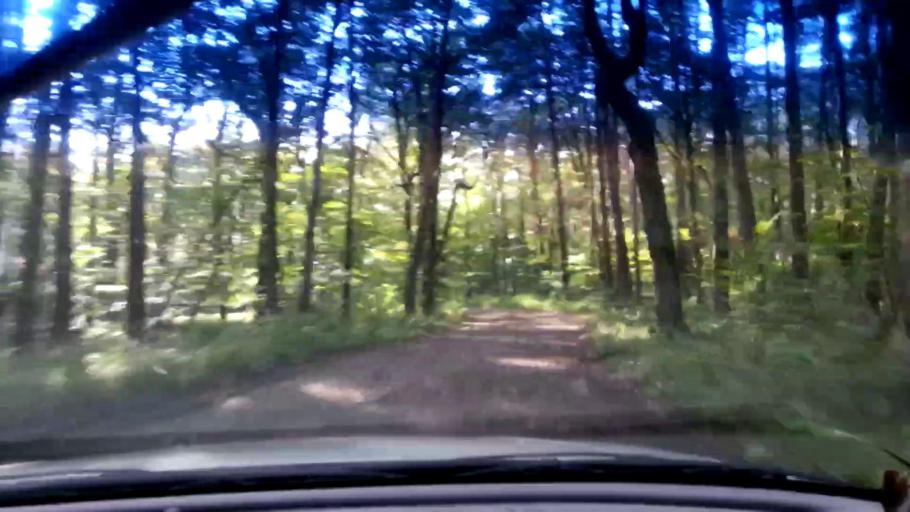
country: DE
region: Bavaria
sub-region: Upper Franconia
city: Lauter
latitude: 49.9579
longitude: 10.7820
